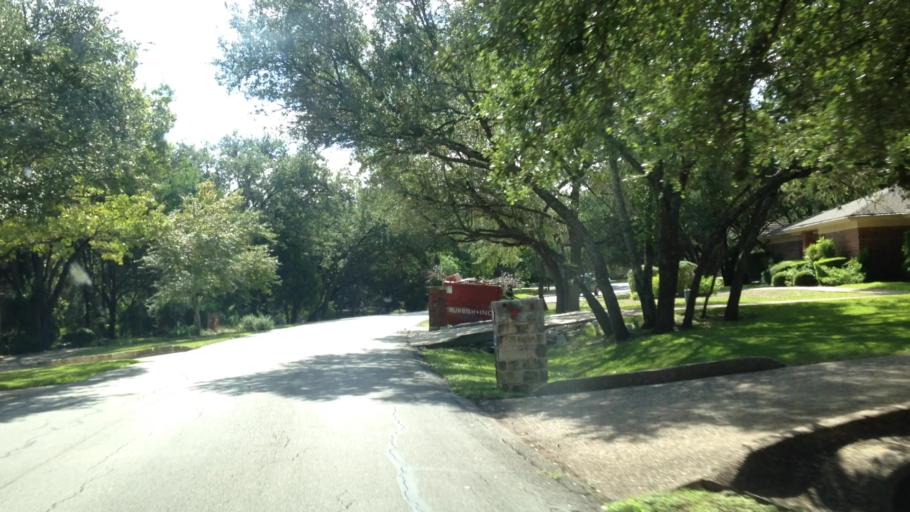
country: US
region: Texas
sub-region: Travis County
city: Lakeway
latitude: 30.3609
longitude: -97.9701
